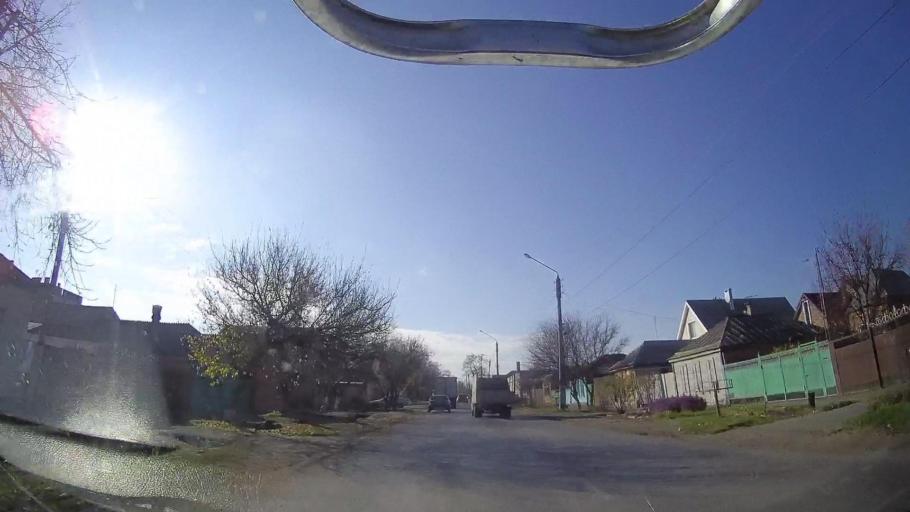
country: RU
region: Rostov
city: Bataysk
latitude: 47.1252
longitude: 39.6910
